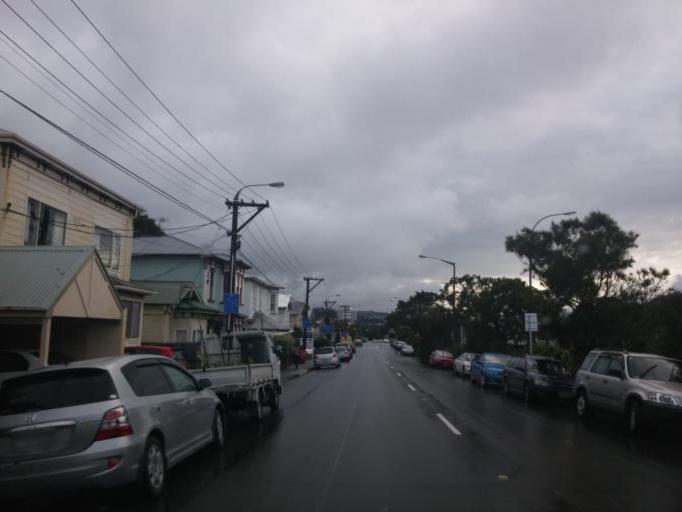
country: NZ
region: Wellington
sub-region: Wellington City
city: Wellington
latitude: -41.2728
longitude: 174.7762
